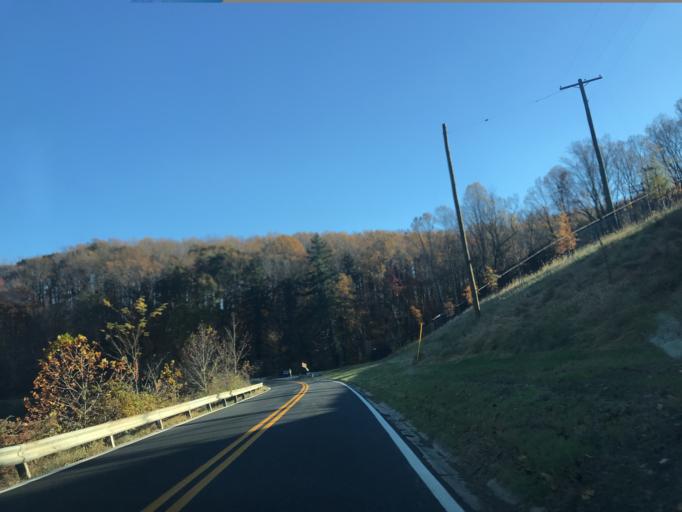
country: US
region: Maryland
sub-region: Baltimore County
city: Carney
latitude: 39.4264
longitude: -76.5447
